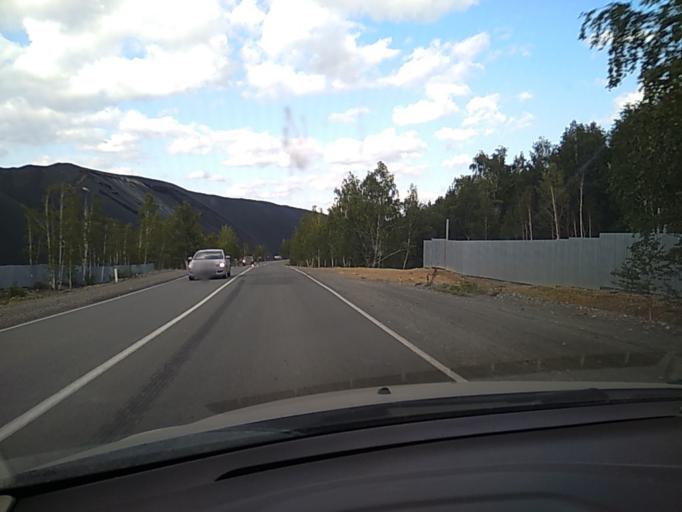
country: RU
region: Chelyabinsk
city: Karabash
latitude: 55.4941
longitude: 60.2459
